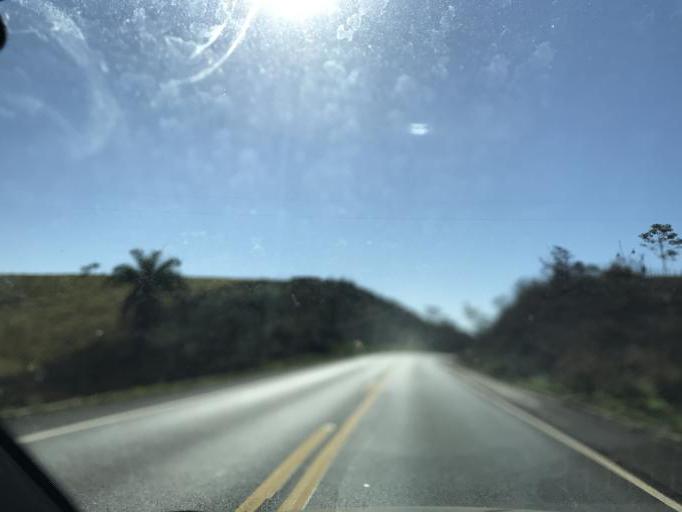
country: BR
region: Minas Gerais
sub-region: Bambui
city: Bambui
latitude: -19.8467
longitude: -45.9990
